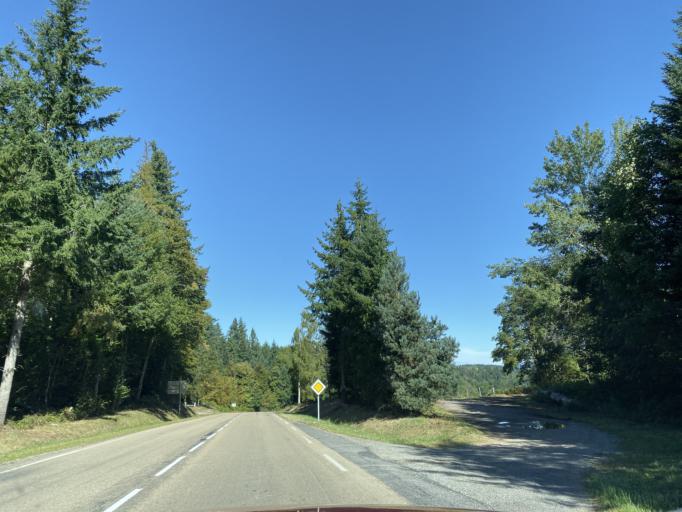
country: FR
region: Rhone-Alpes
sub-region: Departement de la Loire
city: Noiretable
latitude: 45.8236
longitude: 3.7758
